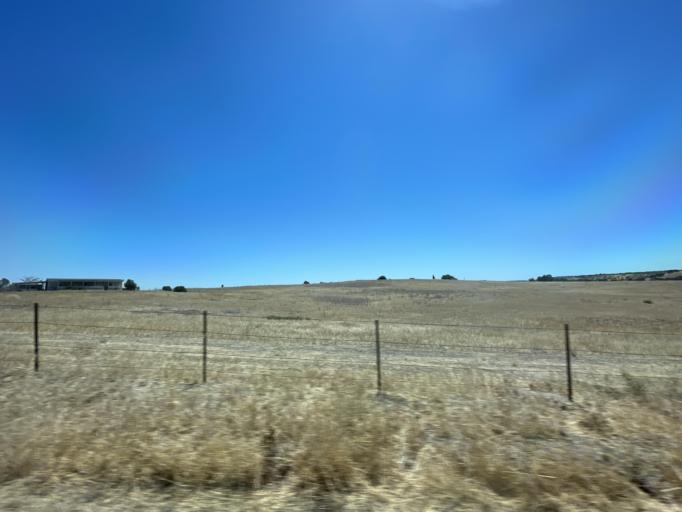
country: US
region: California
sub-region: San Luis Obispo County
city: Paso Robles
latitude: 35.6433
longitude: -120.5784
